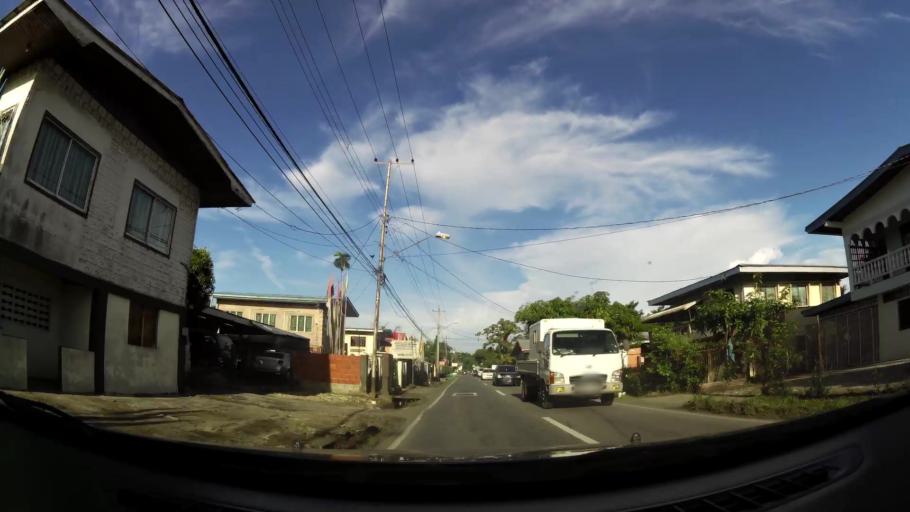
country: TT
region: Chaguanas
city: Chaguanas
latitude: 10.5496
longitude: -61.3584
